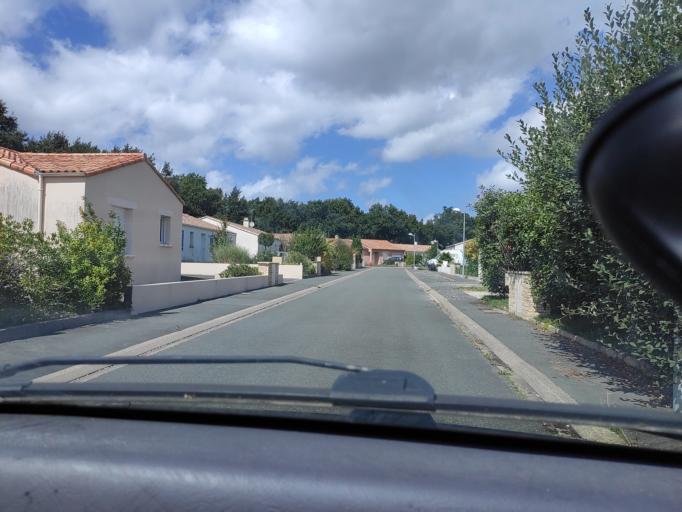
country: FR
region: Pays de la Loire
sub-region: Departement de la Vendee
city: Mouilleron-le-Captif
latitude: 46.6900
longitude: -1.4539
